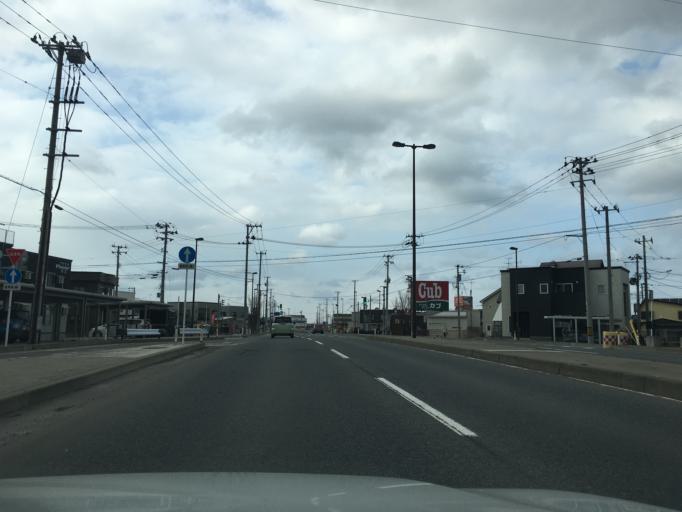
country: JP
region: Aomori
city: Aomori Shi
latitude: 40.8281
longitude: 140.7034
